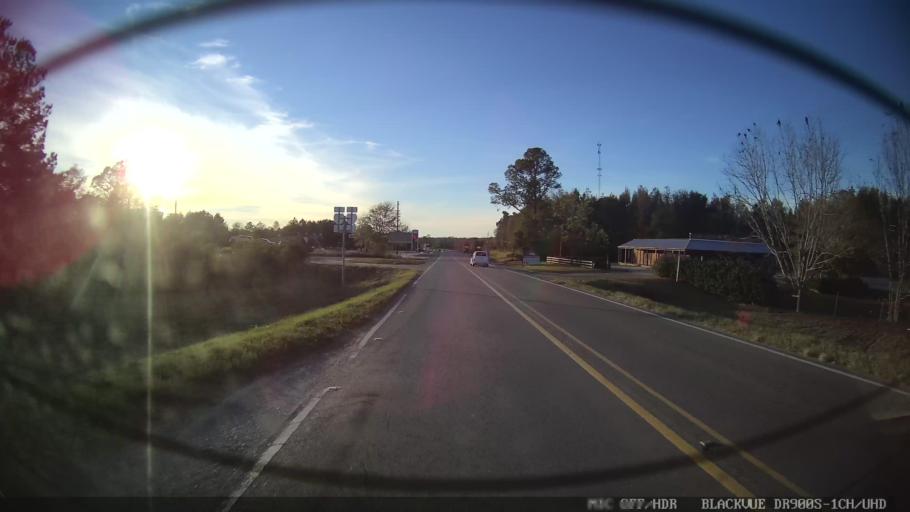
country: US
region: Mississippi
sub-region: Lamar County
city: Lumberton
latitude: 31.0011
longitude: -89.4201
